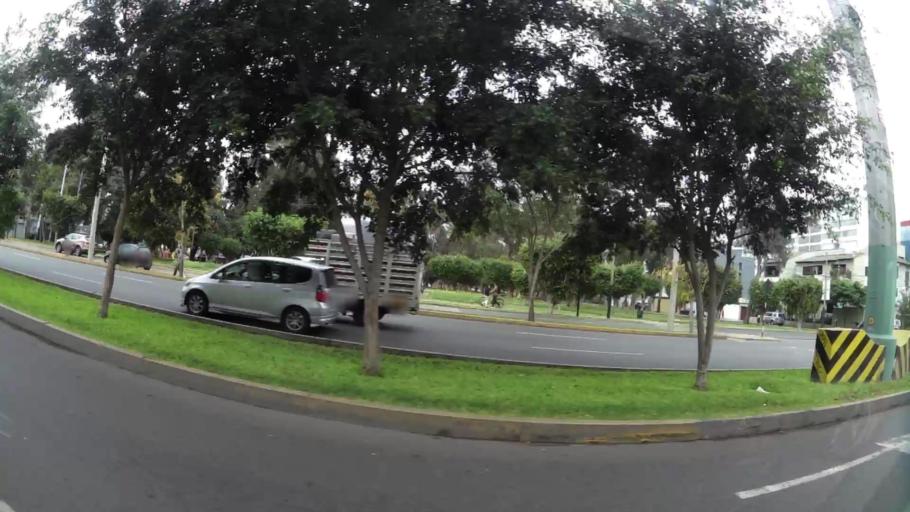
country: PE
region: Lima
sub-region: Lima
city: Surco
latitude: -12.1109
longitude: -76.9883
